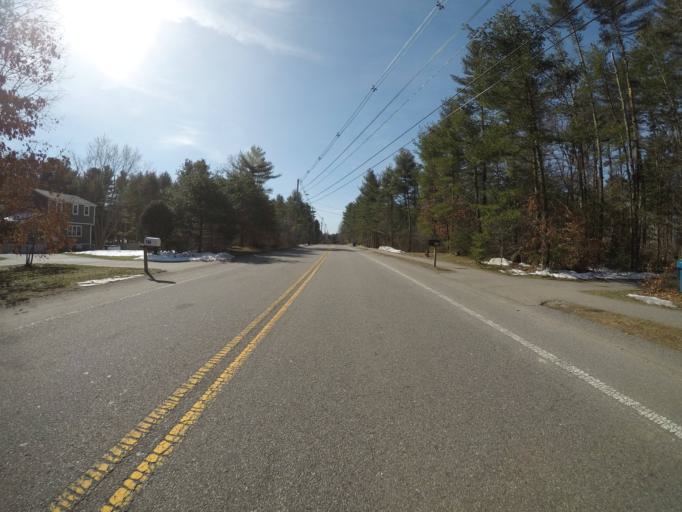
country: US
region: Massachusetts
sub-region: Bristol County
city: Easton
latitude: 42.0029
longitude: -71.1466
